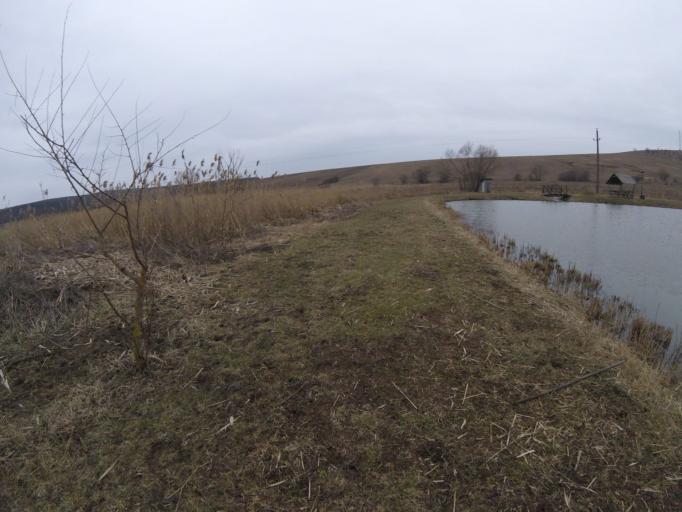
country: HU
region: Borsod-Abauj-Zemplen
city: Rudabanya
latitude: 48.4438
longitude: 20.6098
